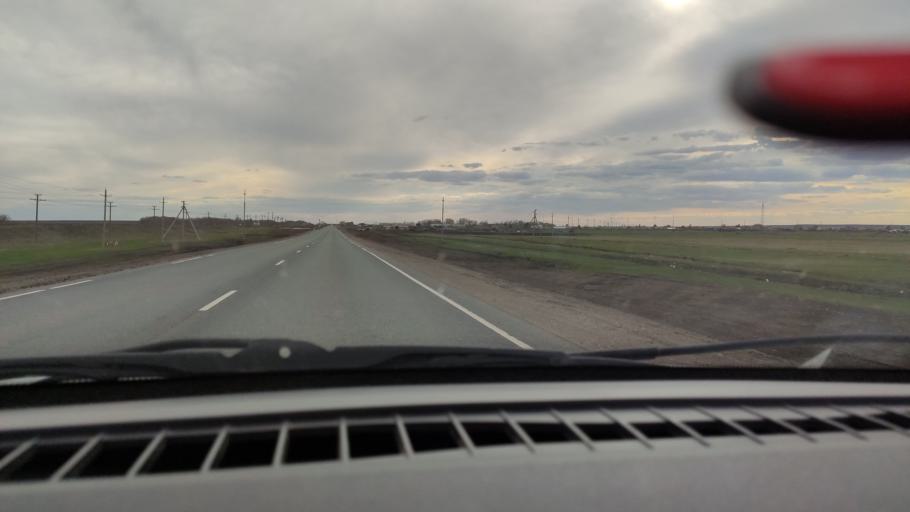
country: RU
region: Bashkortostan
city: Mayachnyy
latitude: 52.3603
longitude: 55.5885
